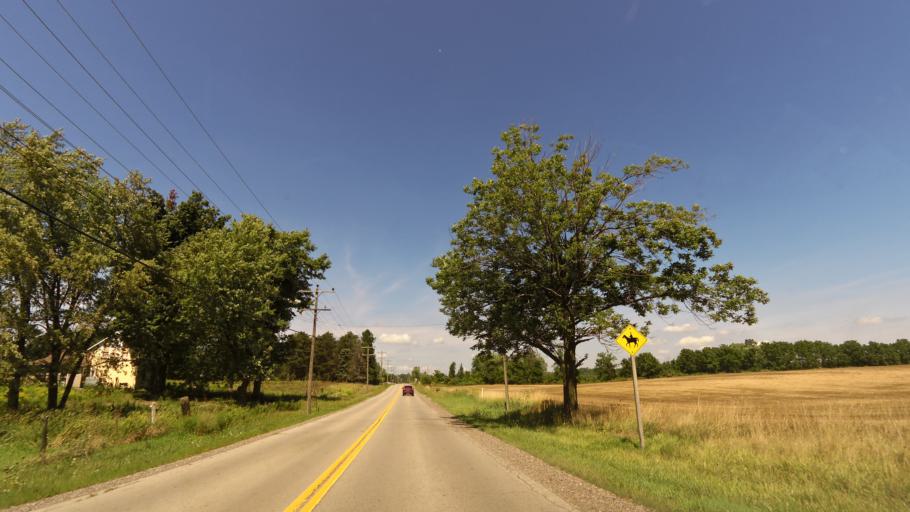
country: CA
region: Ontario
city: Ancaster
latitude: 43.1727
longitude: -79.9731
